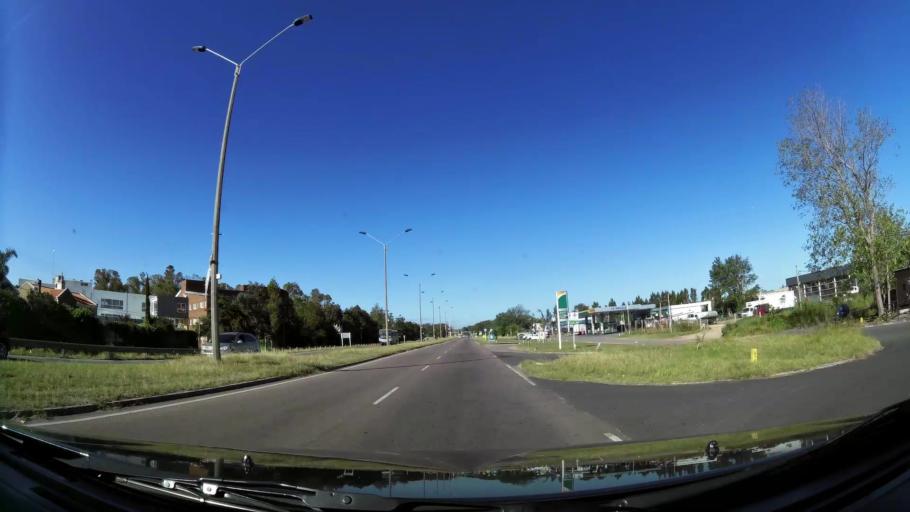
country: UY
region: Canelones
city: Barra de Carrasco
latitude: -34.8720
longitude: -56.0299
